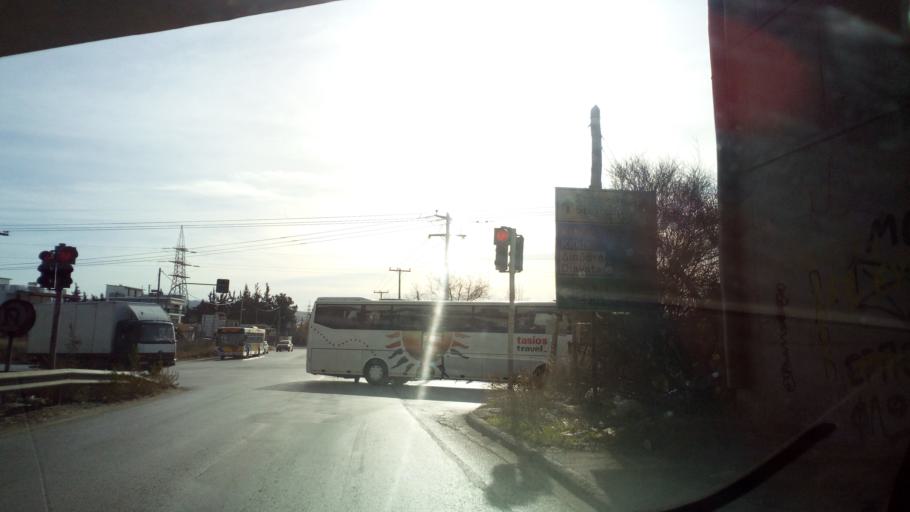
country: GR
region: Central Macedonia
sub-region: Nomos Thessalonikis
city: Efkarpia
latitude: 40.6954
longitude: 22.9328
